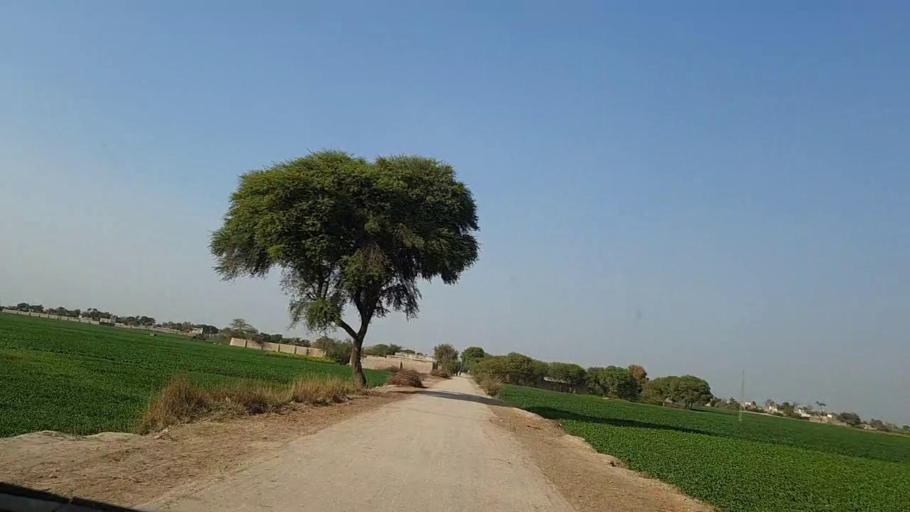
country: PK
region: Sindh
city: Sakrand
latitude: 26.1284
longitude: 68.2381
